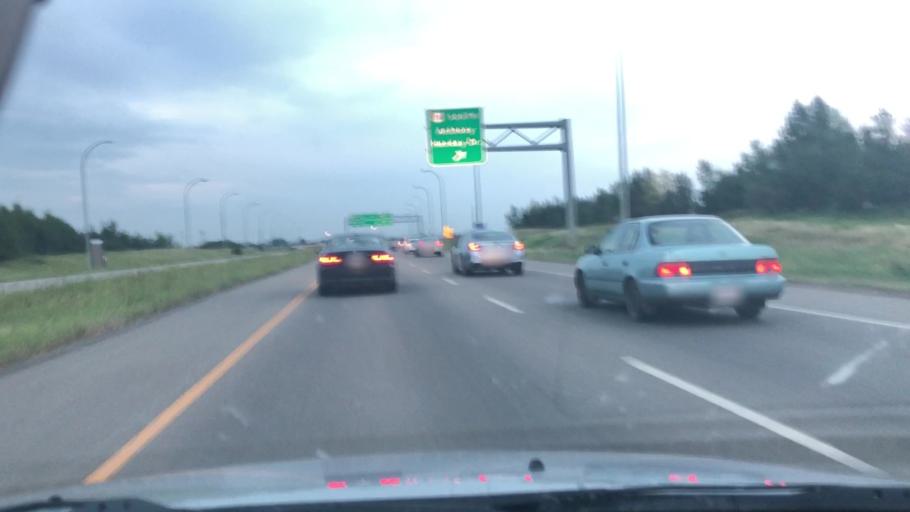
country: CA
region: Alberta
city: St. Albert
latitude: 53.5123
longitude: -113.6713
